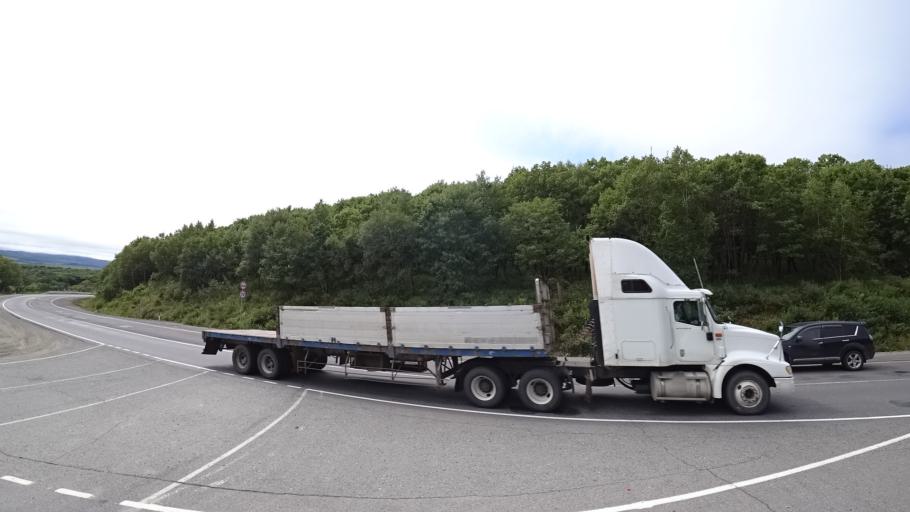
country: RU
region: Primorskiy
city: Lyalichi
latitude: 44.1000
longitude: 132.4244
